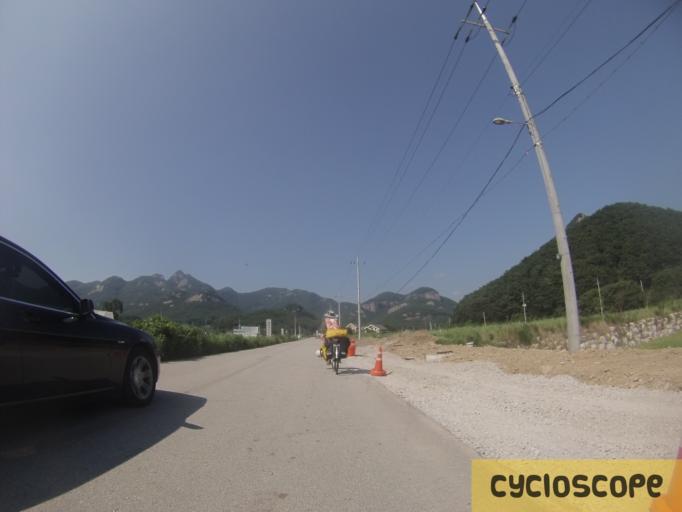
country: KR
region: Jeollabuk-do
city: Puan
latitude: 35.6464
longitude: 126.5066
